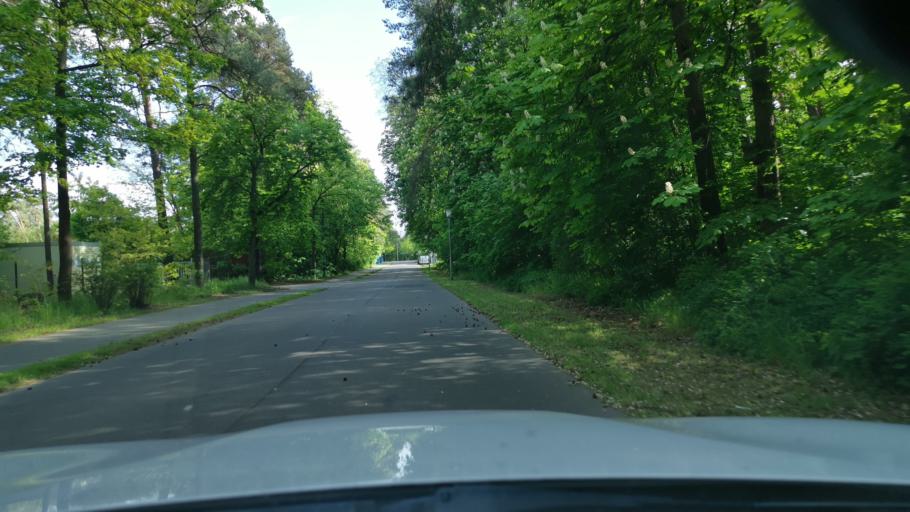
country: DE
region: Brandenburg
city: Niedergorsdorf
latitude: 52.0062
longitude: 12.9942
